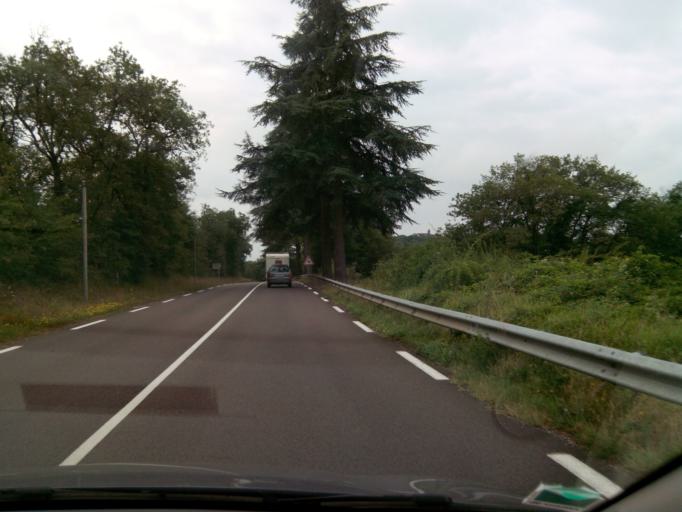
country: FR
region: Midi-Pyrenees
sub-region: Departement du Lot
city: Souillac
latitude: 44.9392
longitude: 1.4931
